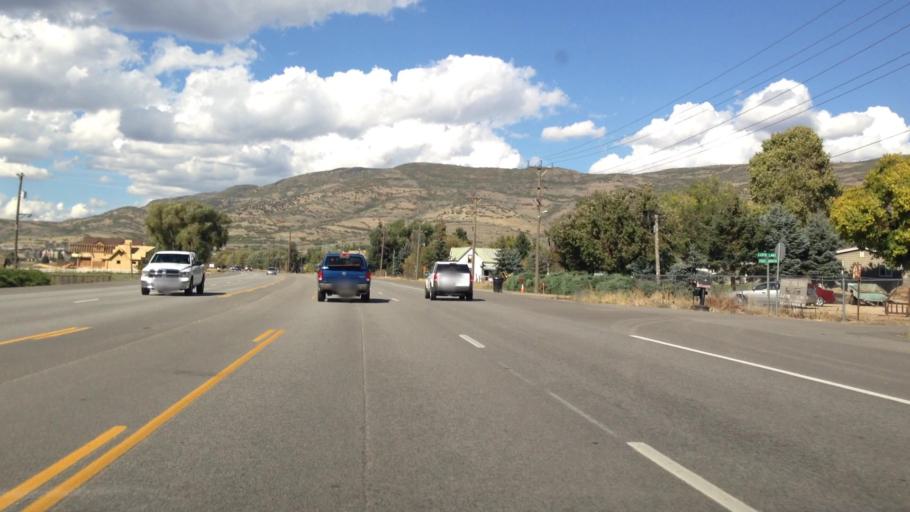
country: US
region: Utah
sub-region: Wasatch County
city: Heber
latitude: 40.5259
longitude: -111.4098
